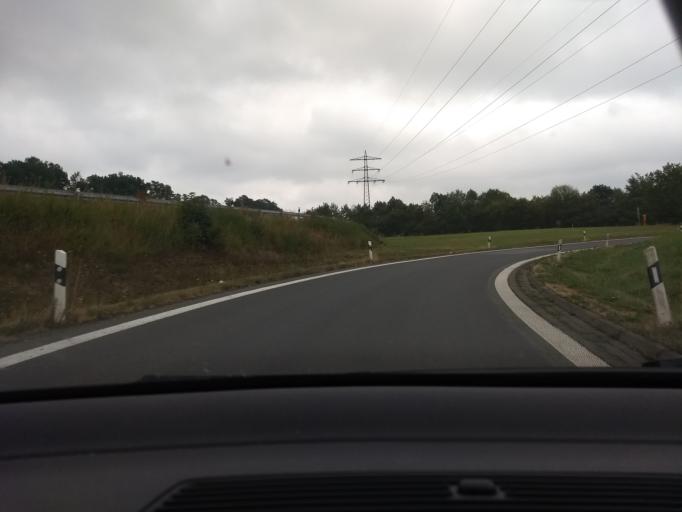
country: DE
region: North Rhine-Westphalia
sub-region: Regierungsbezirk Arnsberg
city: Meschede
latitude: 51.3609
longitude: 8.1887
